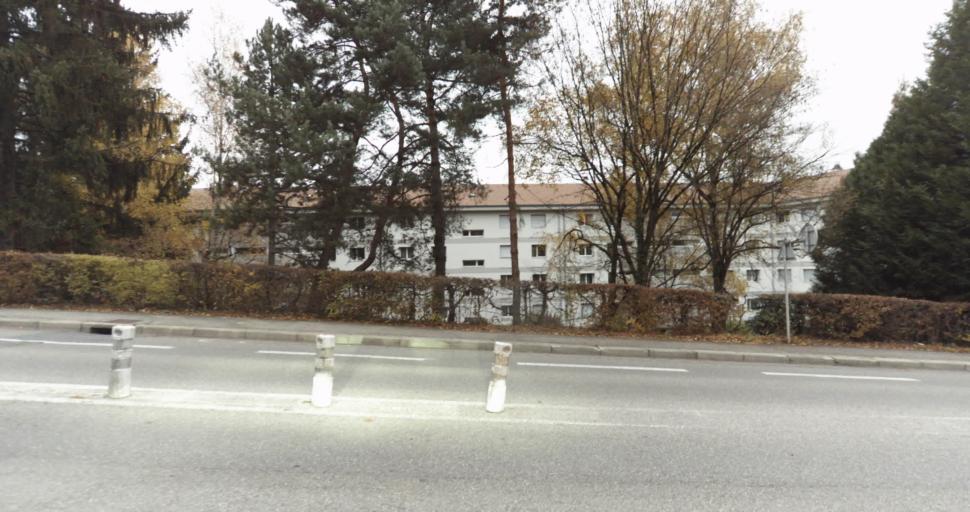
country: FR
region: Rhone-Alpes
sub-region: Departement de la Haute-Savoie
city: Cran-Gevrier
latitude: 45.9023
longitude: 6.1082
